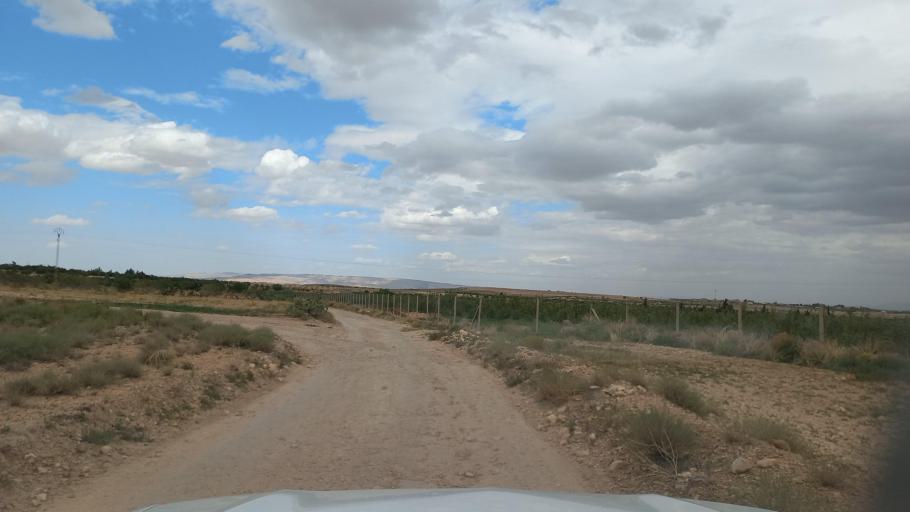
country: TN
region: Al Qasrayn
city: Sbiba
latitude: 35.4356
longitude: 9.0979
